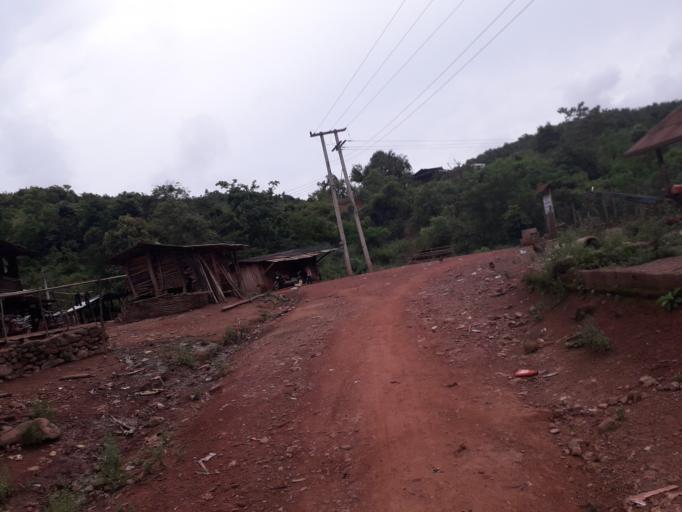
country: CN
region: Yunnan
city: Menglie
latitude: 22.2155
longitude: 101.6571
